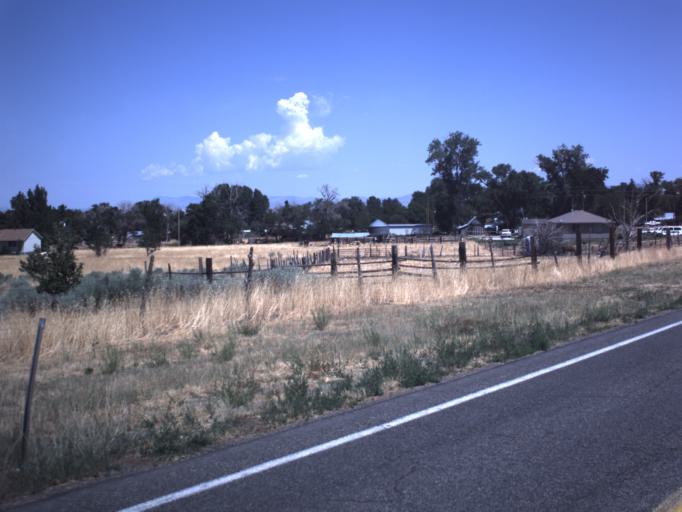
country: US
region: Utah
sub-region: Millard County
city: Delta
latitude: 39.3686
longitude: -112.3369
